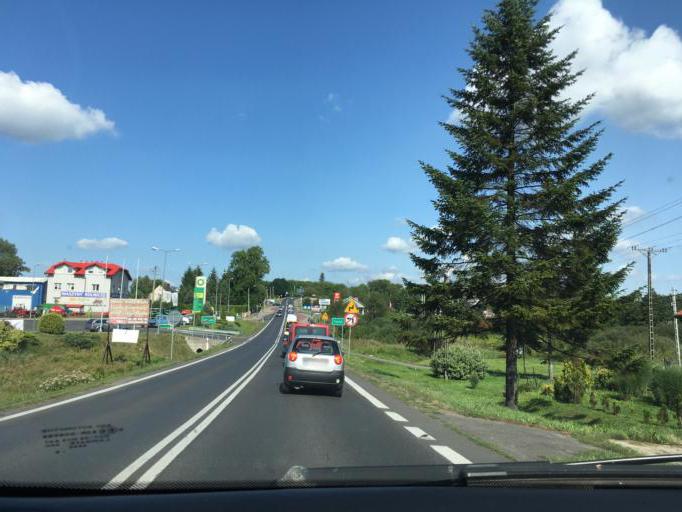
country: PL
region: Subcarpathian Voivodeship
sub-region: Powiat sanocki
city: Sanok
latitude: 49.5349
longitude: 22.2259
